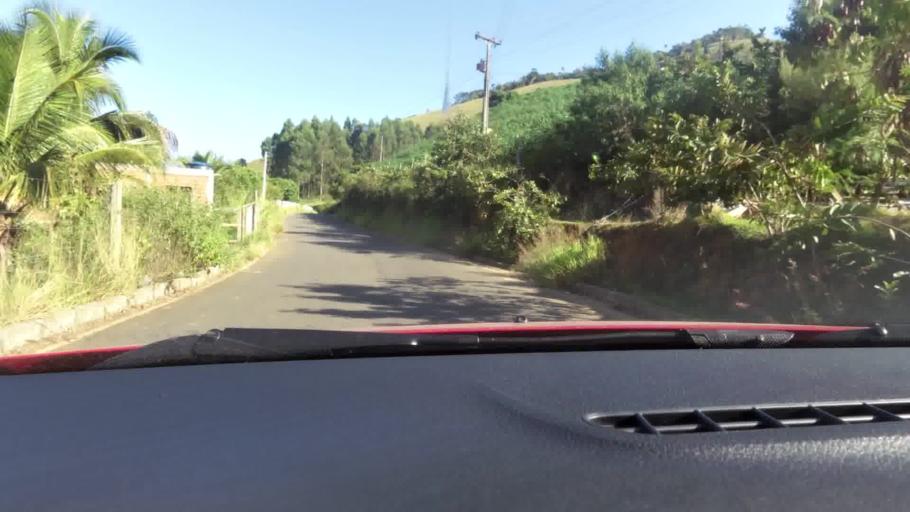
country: BR
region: Espirito Santo
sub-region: Guarapari
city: Guarapari
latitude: -20.5495
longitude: -40.5568
